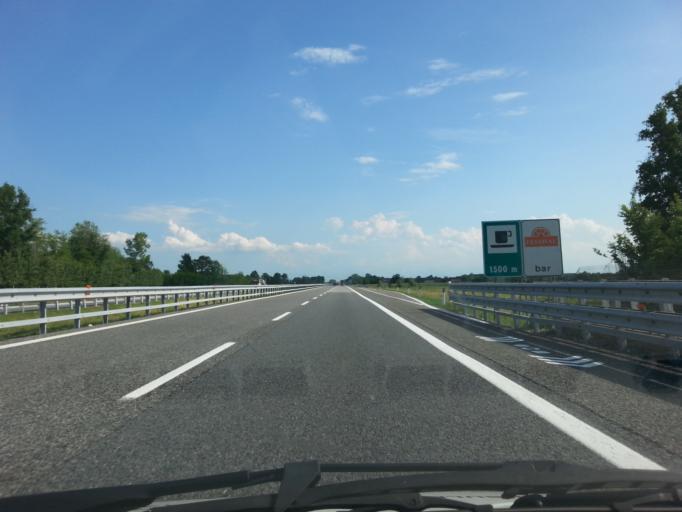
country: IT
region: Piedmont
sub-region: Provincia di Cuneo
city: Sanfre
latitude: 44.7192
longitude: 7.7587
